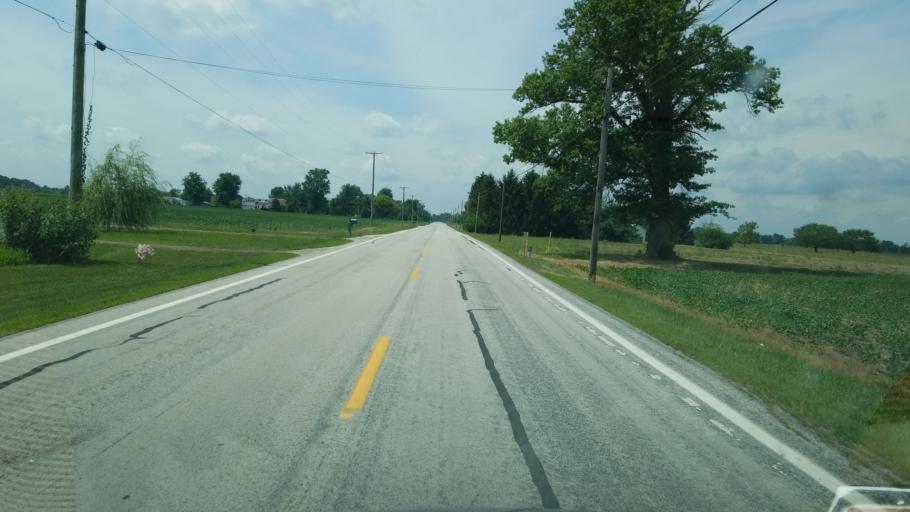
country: US
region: Ohio
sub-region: Hancock County
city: Arlington
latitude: 40.8919
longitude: -83.6267
